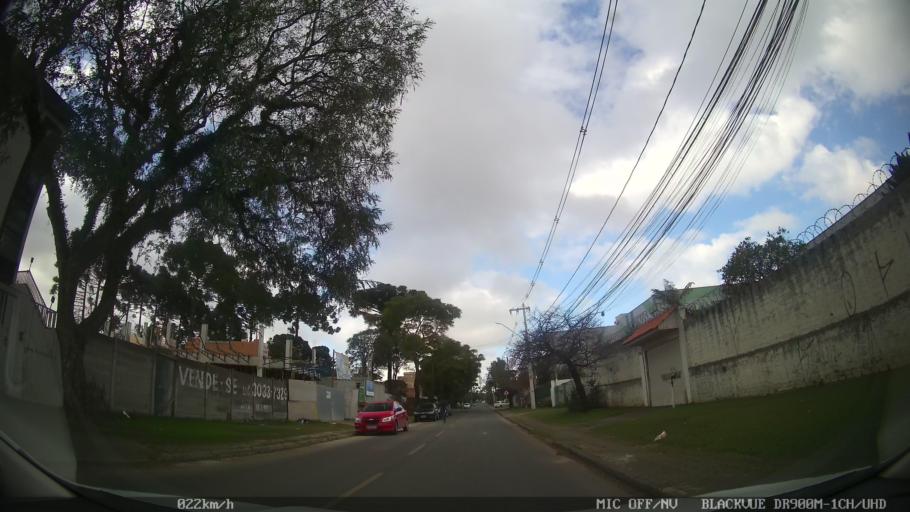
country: BR
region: Parana
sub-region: Pinhais
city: Pinhais
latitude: -25.4358
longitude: -49.1940
